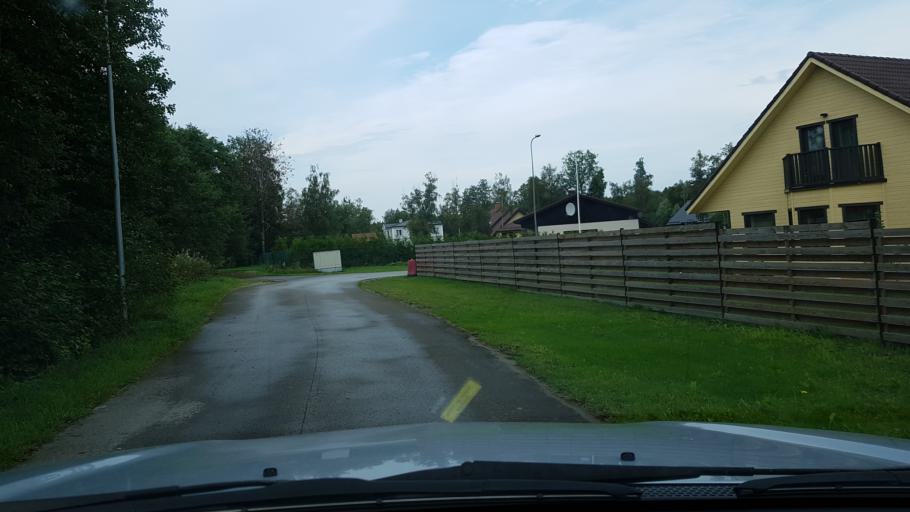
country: EE
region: Harju
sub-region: Rae vald
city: Jueri
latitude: 59.3756
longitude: 24.9434
